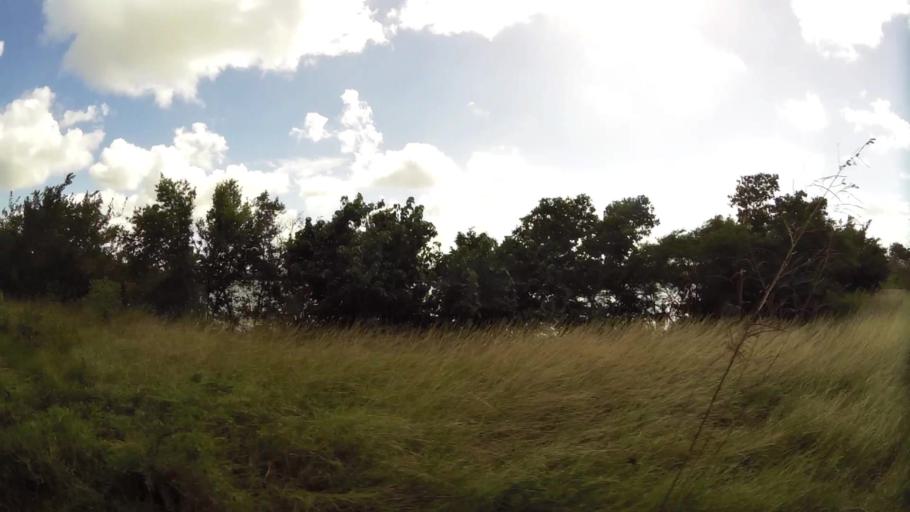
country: AG
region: Saint John
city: Saint John's
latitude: 17.1443
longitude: -61.8567
